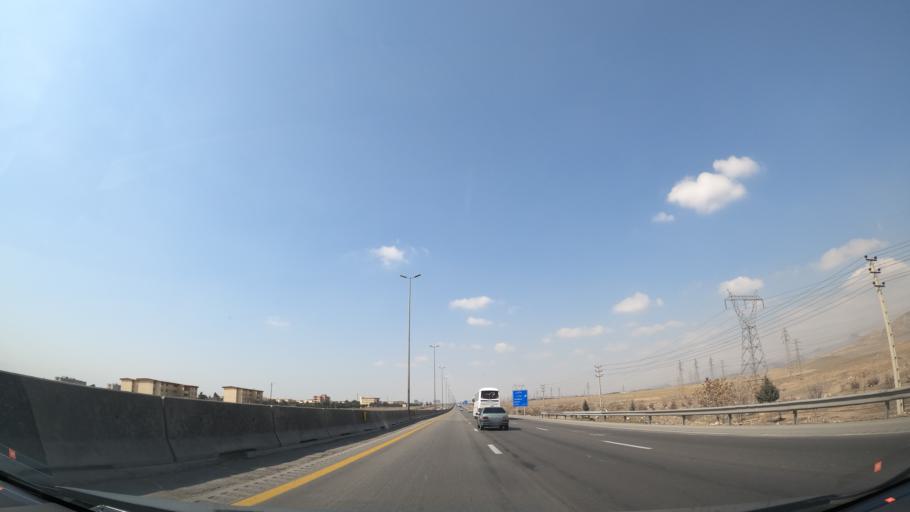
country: IR
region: Qazvin
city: Abyek
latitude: 36.0651
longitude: 50.4891
